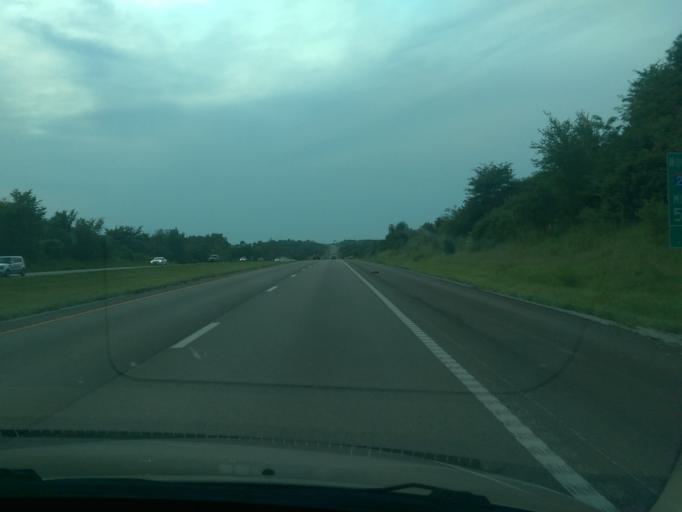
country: US
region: Missouri
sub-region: Andrew County
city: Country Club Village
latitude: 39.8785
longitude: -94.8435
